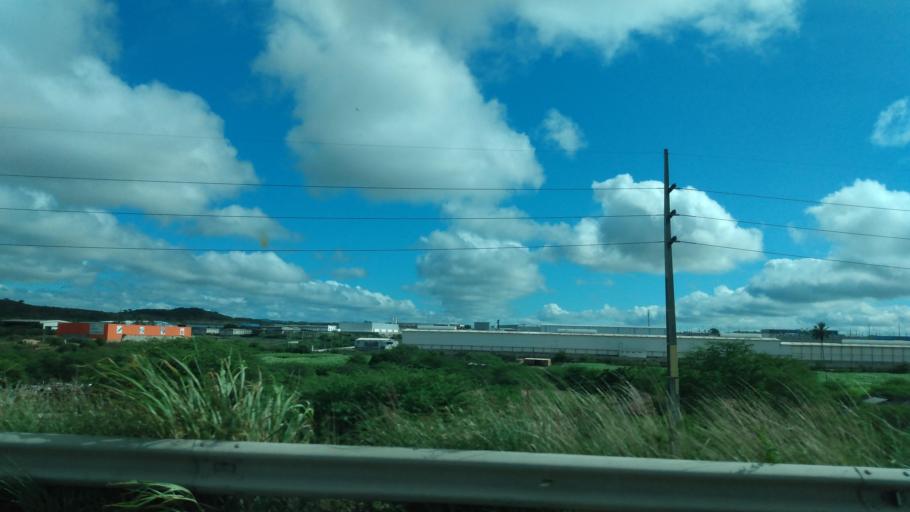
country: BR
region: Pernambuco
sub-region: Caruaru
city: Caruaru
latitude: -8.3051
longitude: -36.0124
